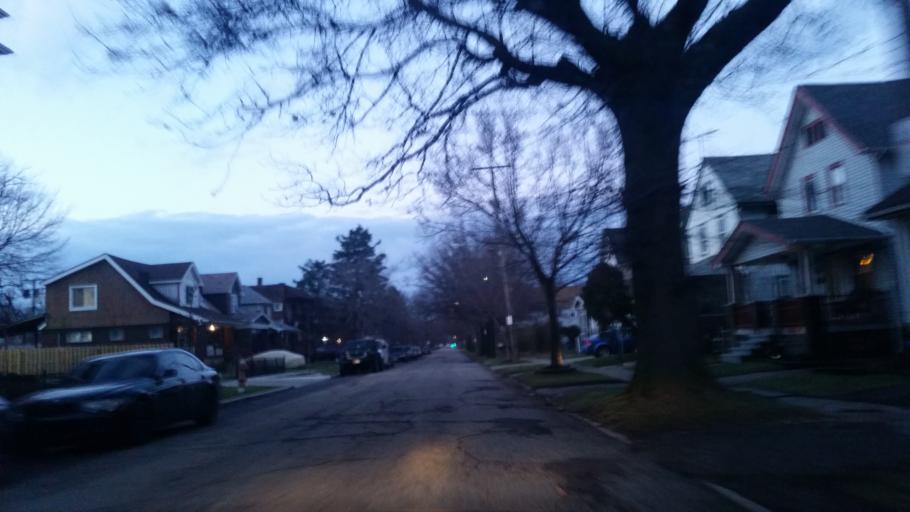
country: US
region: Ohio
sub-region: Cuyahoga County
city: Lakewood
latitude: 41.4776
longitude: -81.7675
